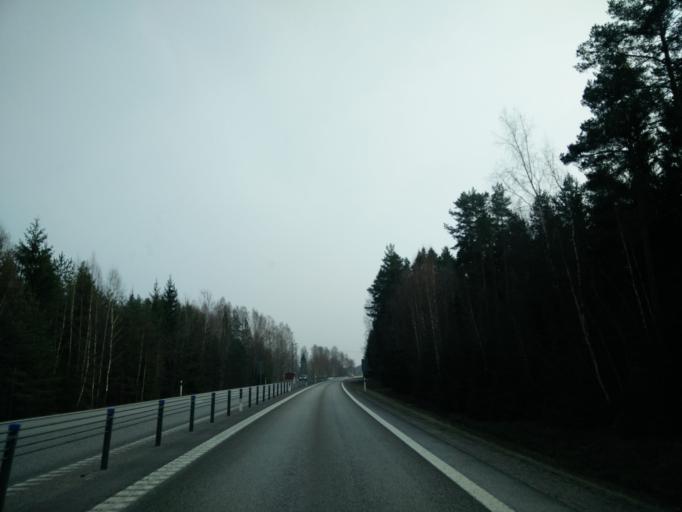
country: SE
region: Vaermland
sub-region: Forshaga Kommun
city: Forshaga
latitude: 59.4660
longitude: 13.4149
